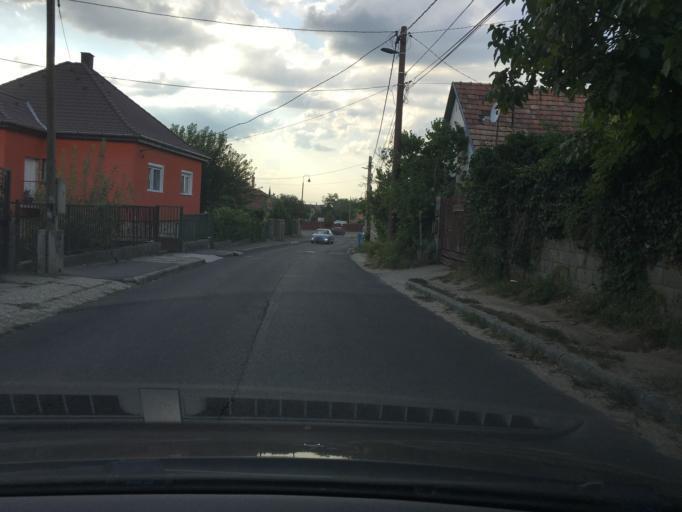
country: HU
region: Pest
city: Veresegyhaz
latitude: 47.6560
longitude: 19.2902
